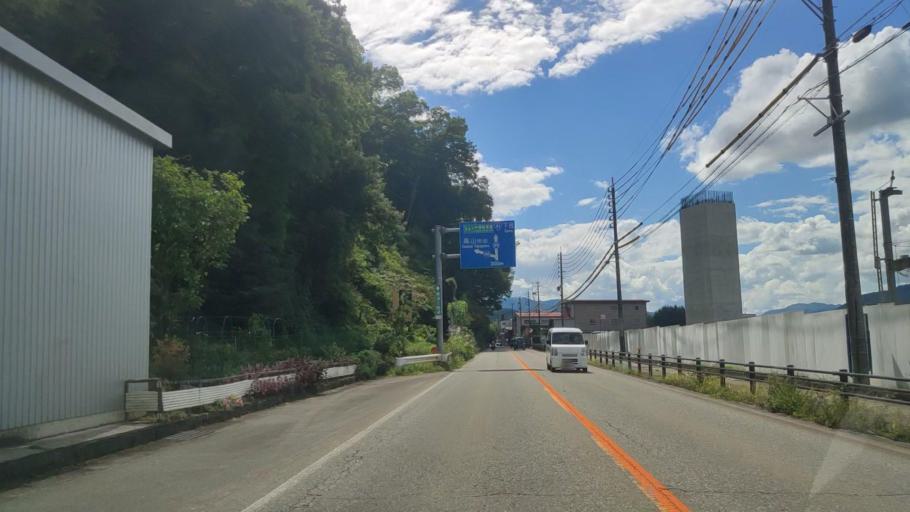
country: JP
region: Gifu
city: Takayama
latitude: 36.1735
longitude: 137.2479
